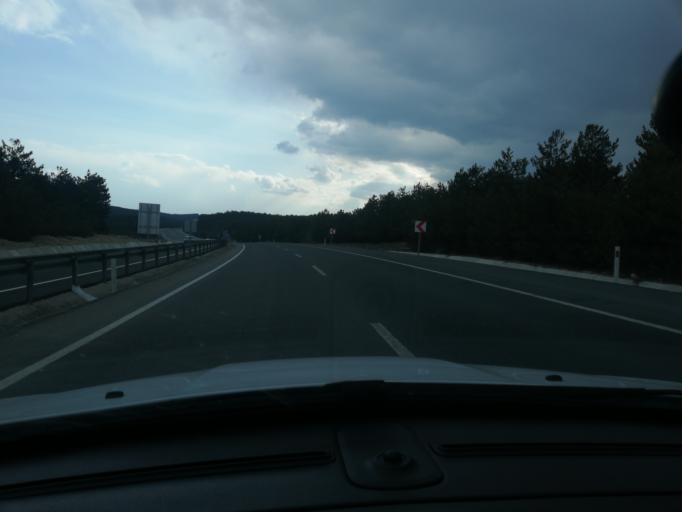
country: TR
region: Kastamonu
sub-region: Cide
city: Kastamonu
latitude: 41.4174
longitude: 33.7686
